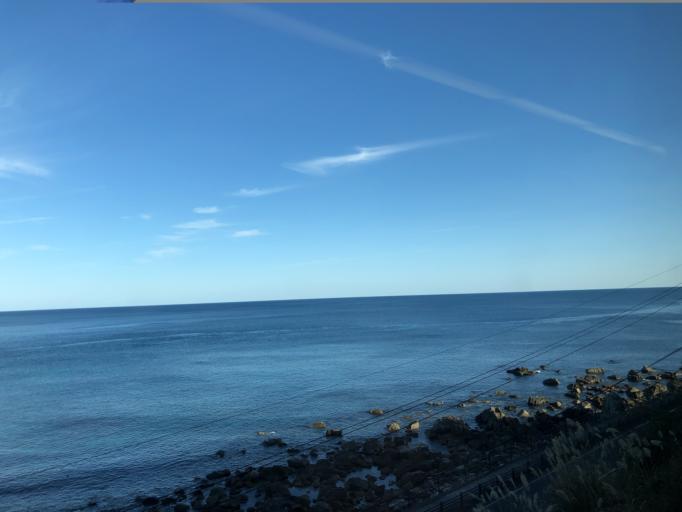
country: JP
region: Kochi
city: Nakamura
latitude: 33.0535
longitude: 133.0972
